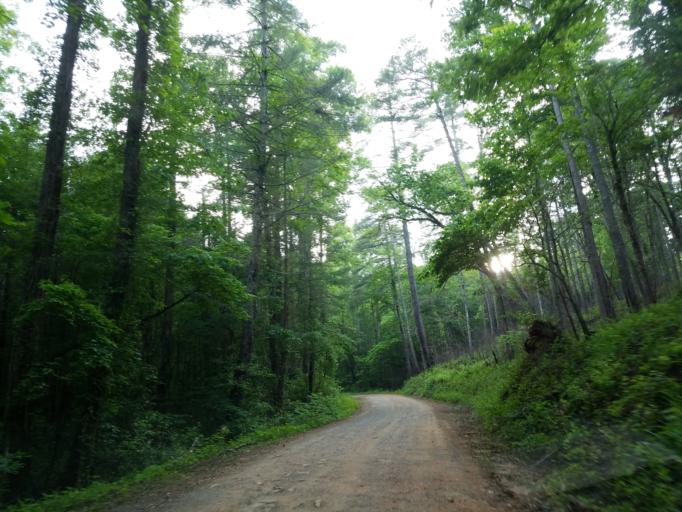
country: US
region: Georgia
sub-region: Lumpkin County
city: Dahlonega
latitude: 34.5877
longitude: -84.1212
